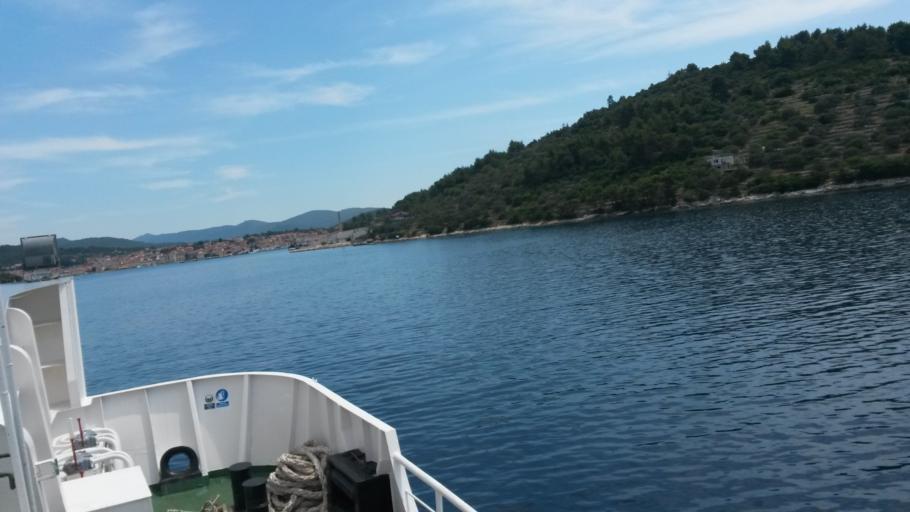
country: HR
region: Dubrovacko-Neretvanska
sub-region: Grad Dubrovnik
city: Vela Luka
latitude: 42.9621
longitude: 16.6966
